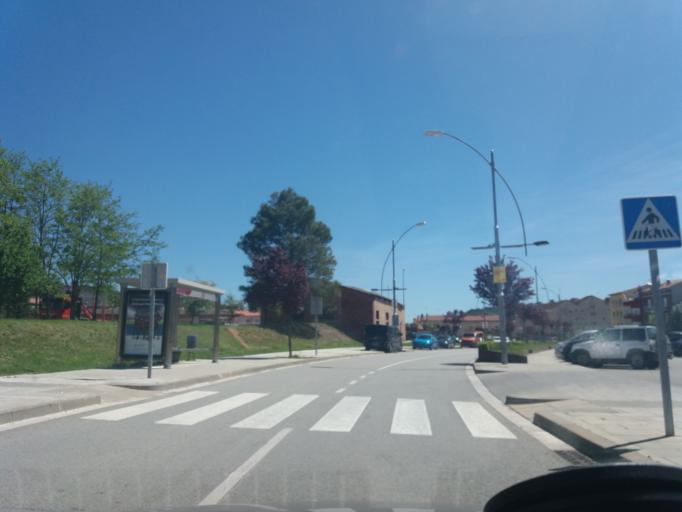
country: ES
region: Catalonia
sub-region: Provincia de Barcelona
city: Avia
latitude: 42.0715
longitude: 1.8702
